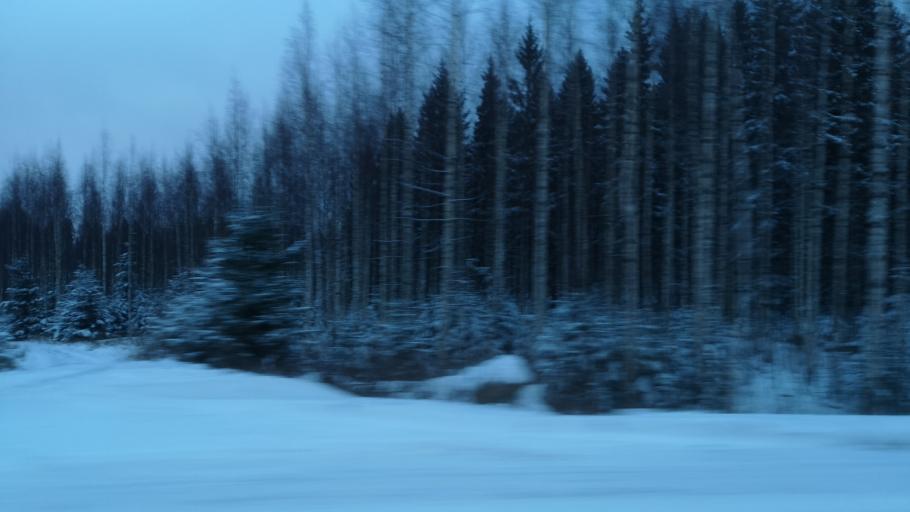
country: FI
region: Southern Savonia
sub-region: Savonlinna
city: Enonkoski
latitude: 62.0757
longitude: 28.7156
